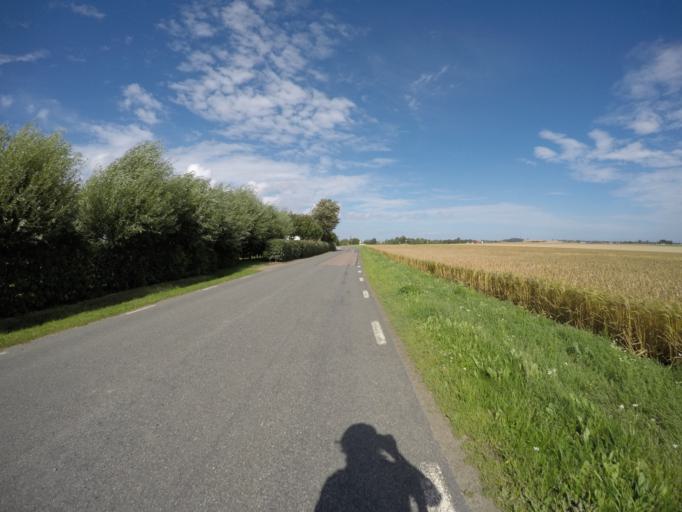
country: SE
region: Skane
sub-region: Simrishamns Kommun
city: Simrishamn
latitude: 55.4924
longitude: 14.1964
